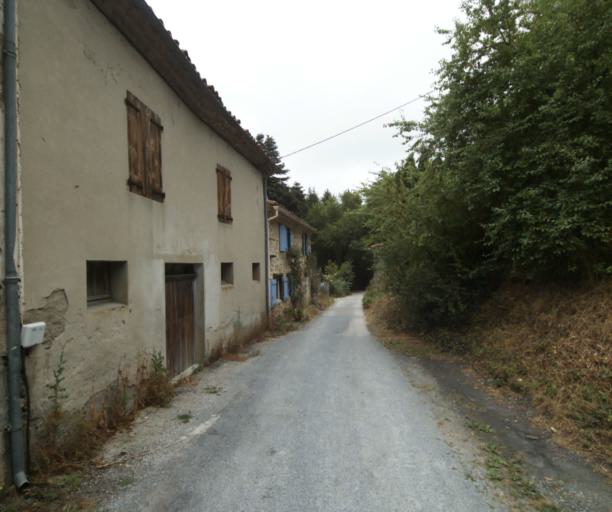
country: FR
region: Midi-Pyrenees
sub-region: Departement du Tarn
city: Soreze
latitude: 43.4094
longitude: 2.0855
